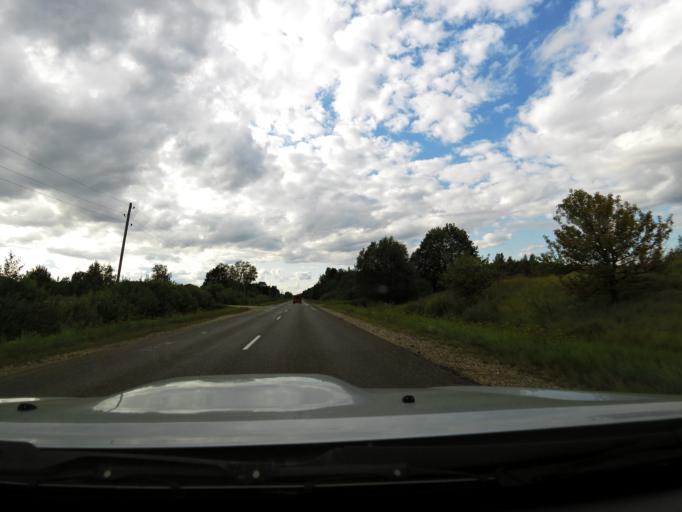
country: LV
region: Akniste
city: Akniste
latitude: 55.9928
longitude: 25.9736
